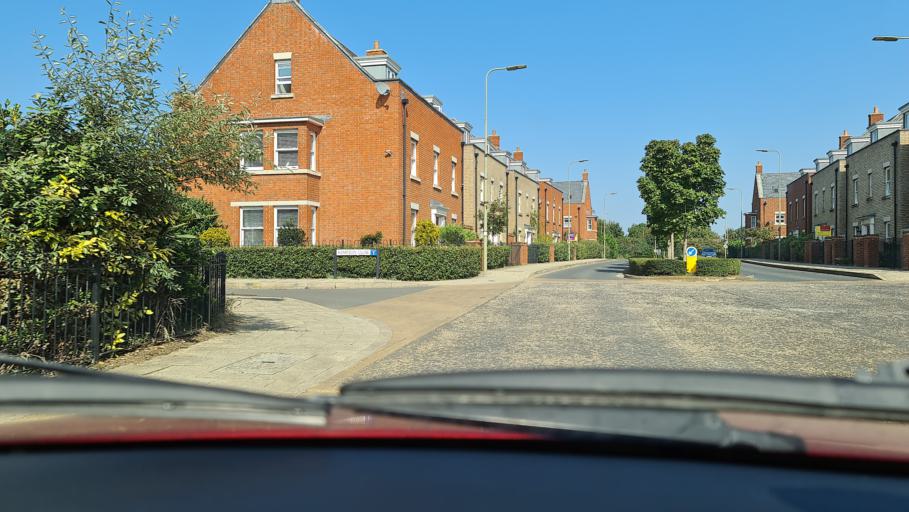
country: GB
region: England
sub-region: Oxfordshire
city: Bicester
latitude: 51.8973
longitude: -1.1745
